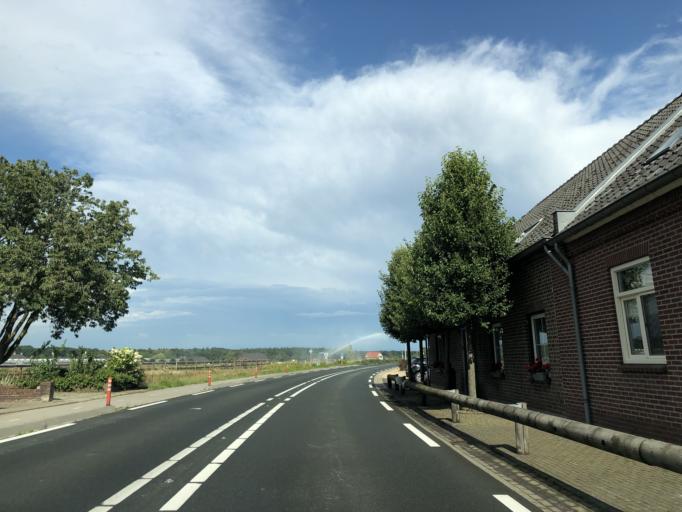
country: NL
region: Limburg
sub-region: Gemeente Gennep
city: Gennep
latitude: 51.7147
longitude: 6.0374
